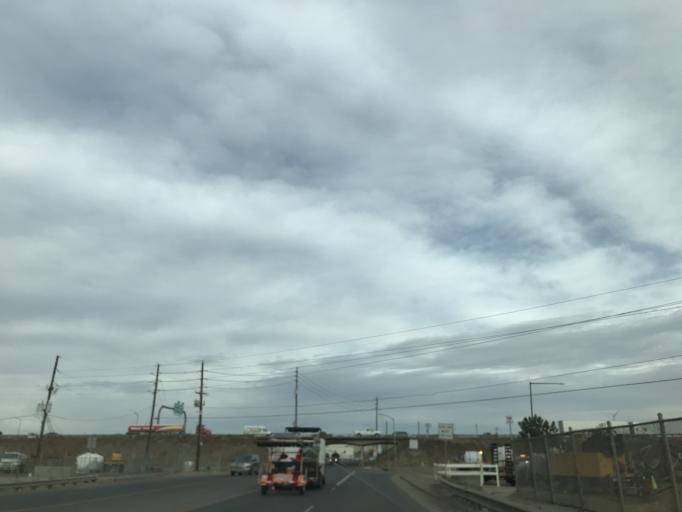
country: US
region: Colorado
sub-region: Adams County
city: Commerce City
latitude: 39.7970
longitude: -104.9321
